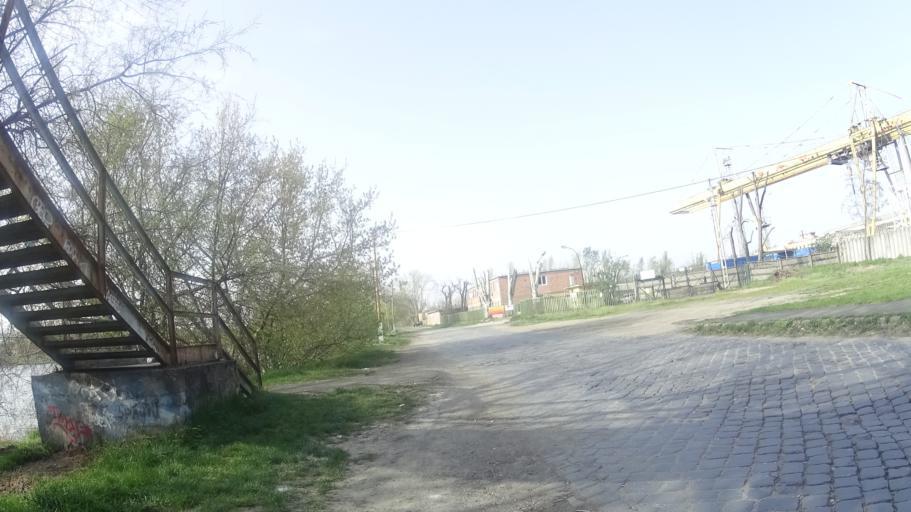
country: HU
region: Budapest
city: Budapest XX. keruelet
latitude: 47.4364
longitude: 19.0896
